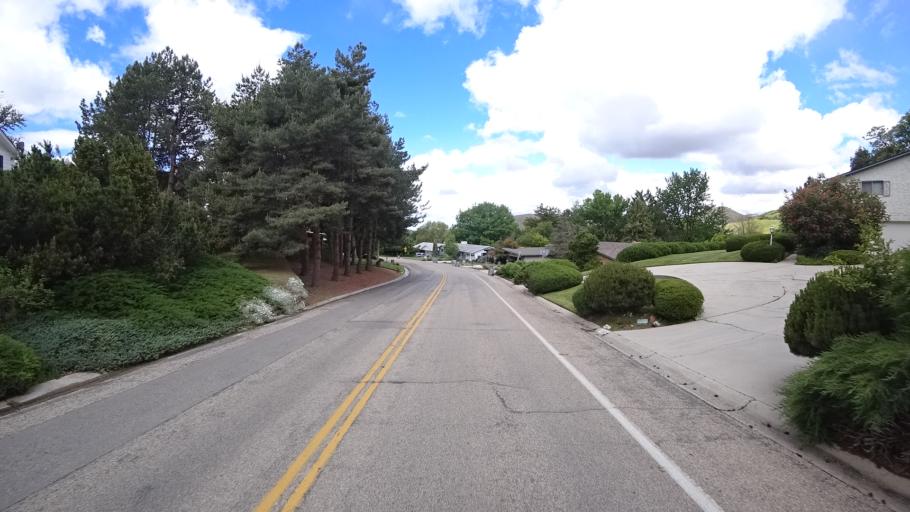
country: US
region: Idaho
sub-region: Ada County
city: Boise
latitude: 43.6463
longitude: -116.1934
